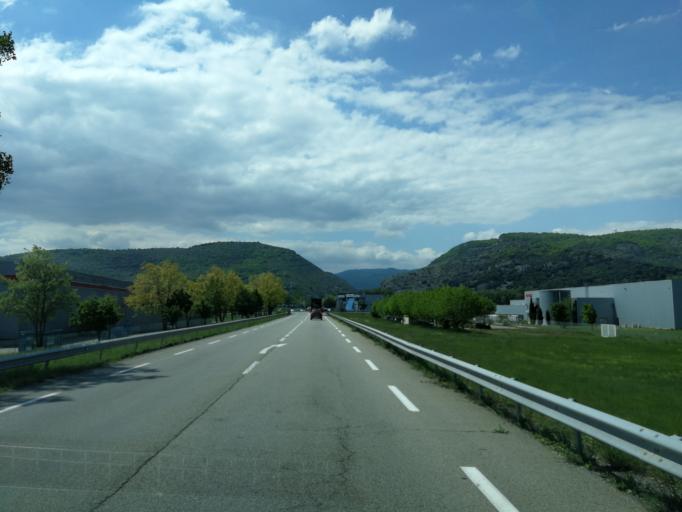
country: FR
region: Rhone-Alpes
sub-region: Departement de l'Ardeche
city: Le Pouzin
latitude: 44.7561
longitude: 4.7642
